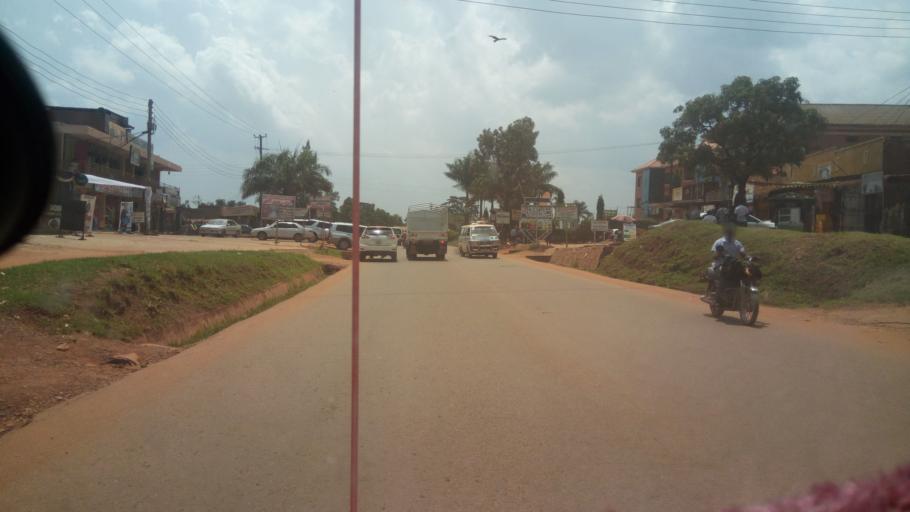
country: UG
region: Central Region
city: Kampala Central Division
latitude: 0.3633
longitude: 32.5292
